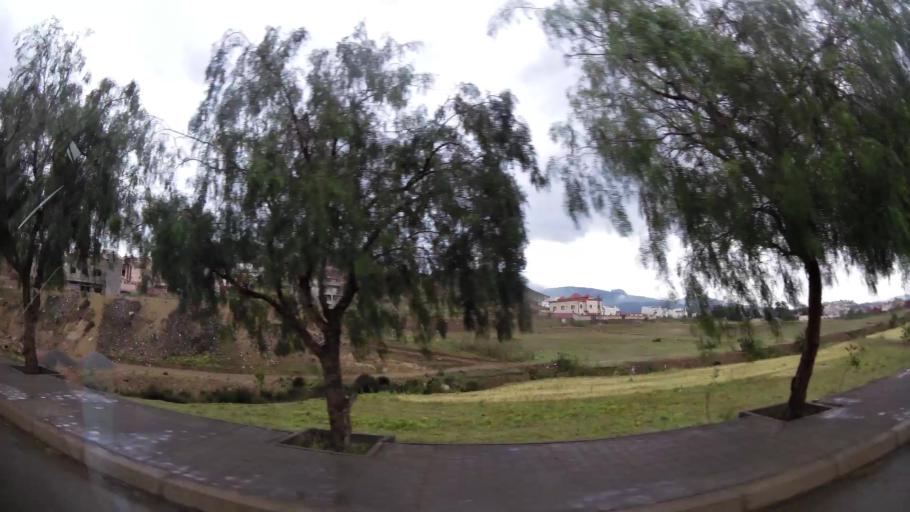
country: MA
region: Oriental
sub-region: Nador
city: Nador
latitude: 35.1459
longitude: -3.0105
